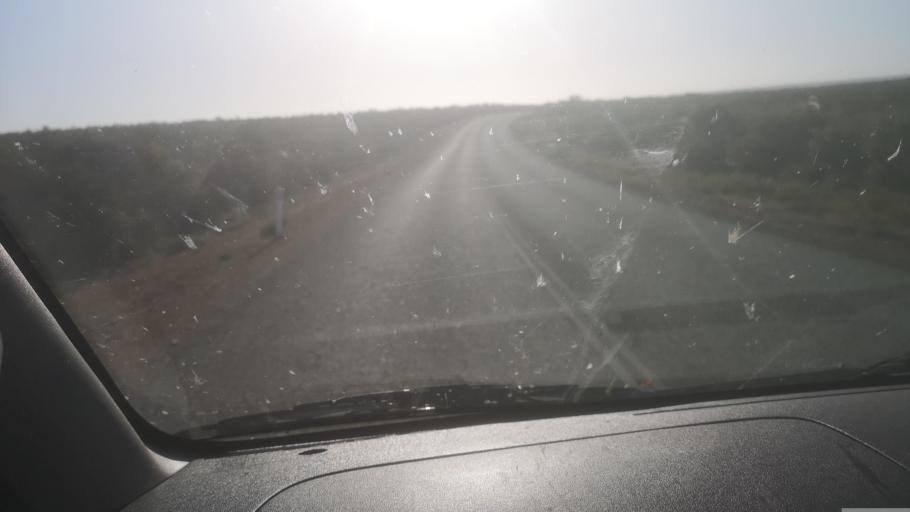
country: AU
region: Western Australia
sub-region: Dandaragan
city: Jurien Bay
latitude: -30.6044
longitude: 115.1452
